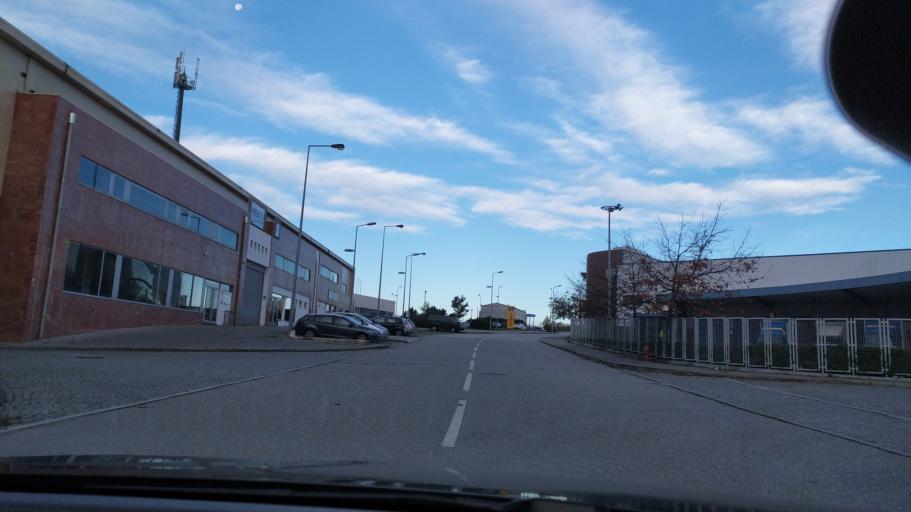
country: PT
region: Porto
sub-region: Matosinhos
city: Santa Cruz do Bispo
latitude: 41.2346
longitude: -8.6633
